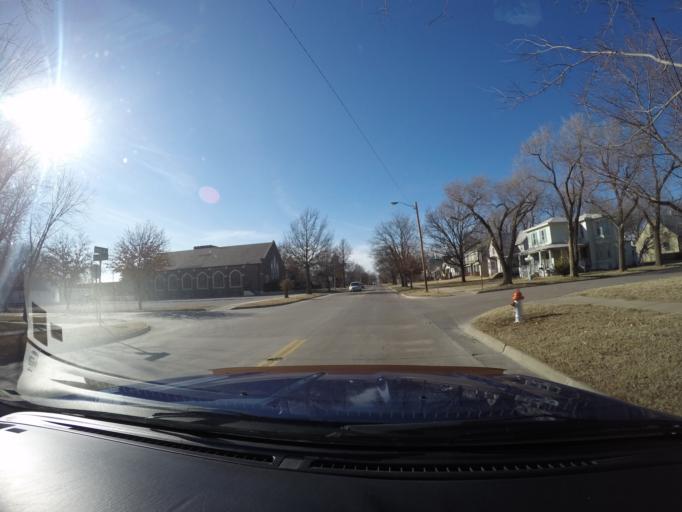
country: US
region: Kansas
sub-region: Harvey County
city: Newton
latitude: 38.0428
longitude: -97.3388
